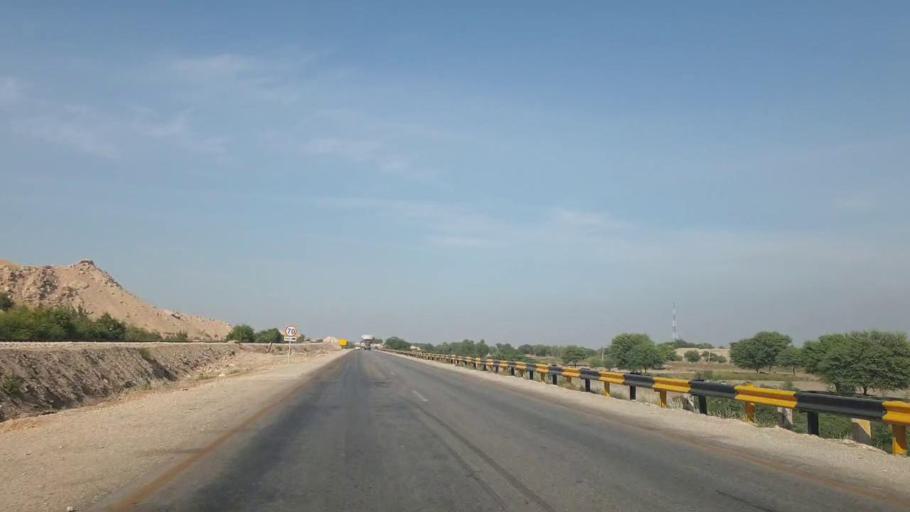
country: PK
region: Sindh
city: Sehwan
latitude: 26.2937
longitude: 67.8944
